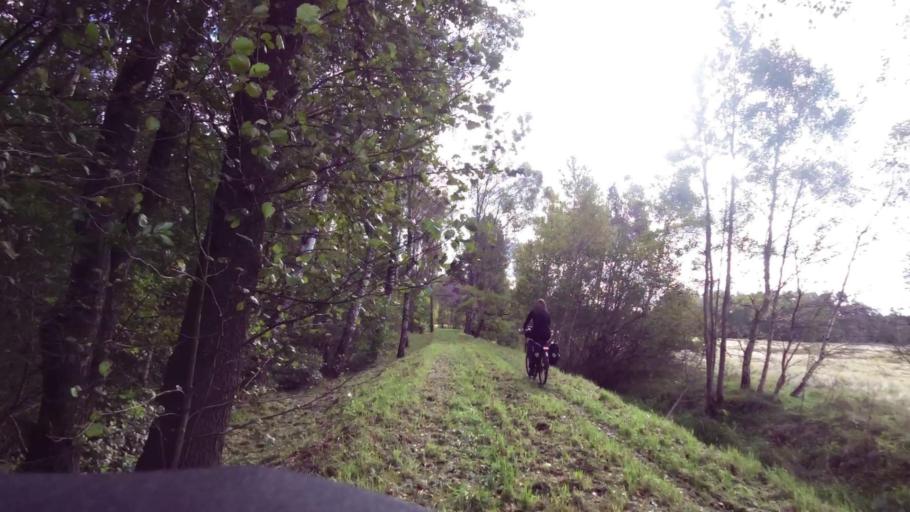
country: PL
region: West Pomeranian Voivodeship
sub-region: Powiat bialogardzki
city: Bialogard
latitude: 53.9938
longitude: 16.0363
